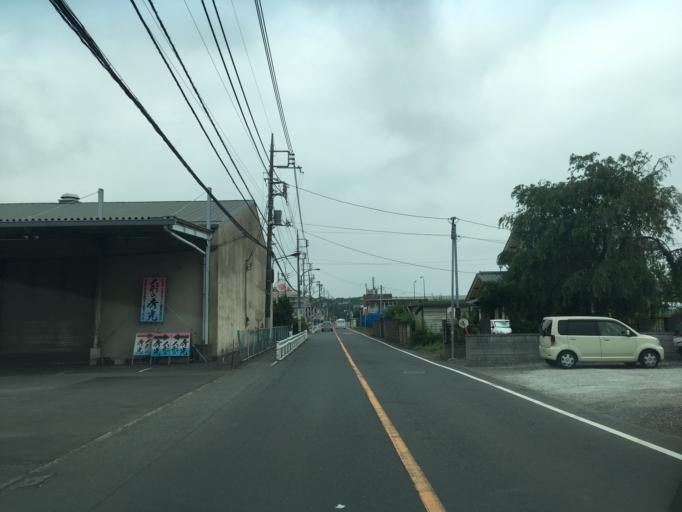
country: JP
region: Tokyo
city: Hino
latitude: 35.7220
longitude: 139.3973
